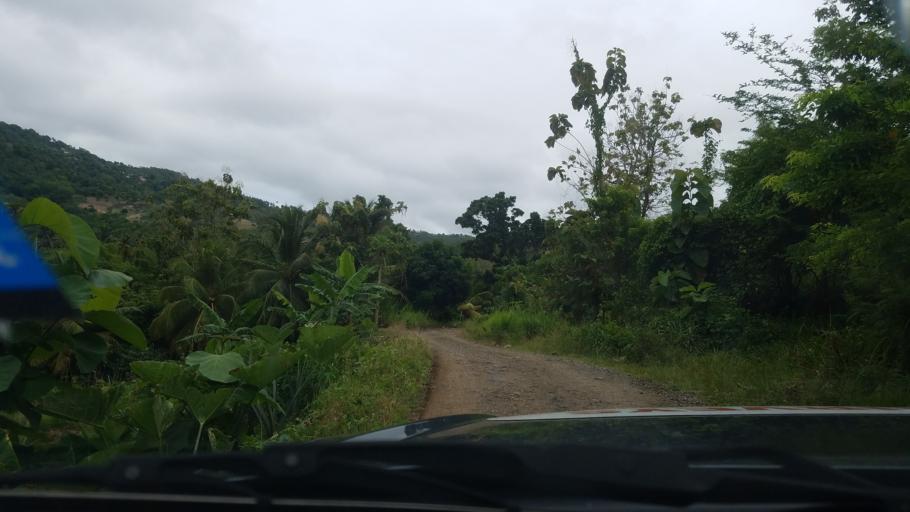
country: LC
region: Castries Quarter
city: Bisee
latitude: 14.0144
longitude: -60.9145
